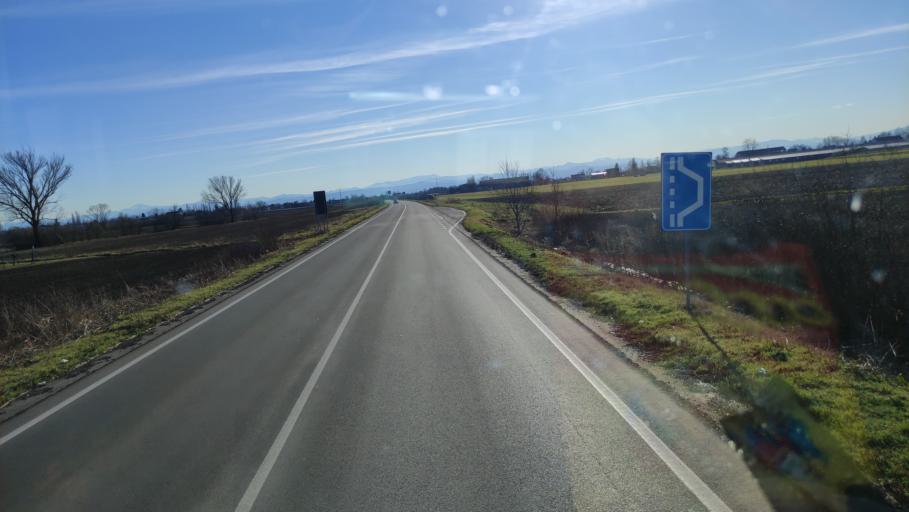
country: IT
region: Emilia-Romagna
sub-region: Provincia di Reggio Emilia
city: Bagnolo in Piano
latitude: 44.8069
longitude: 10.6856
